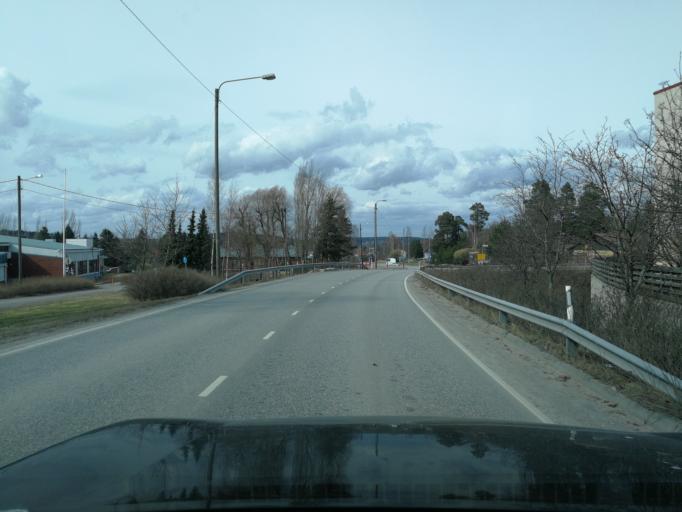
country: FI
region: Uusimaa
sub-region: Helsinki
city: Siuntio
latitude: 60.1365
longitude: 24.2278
